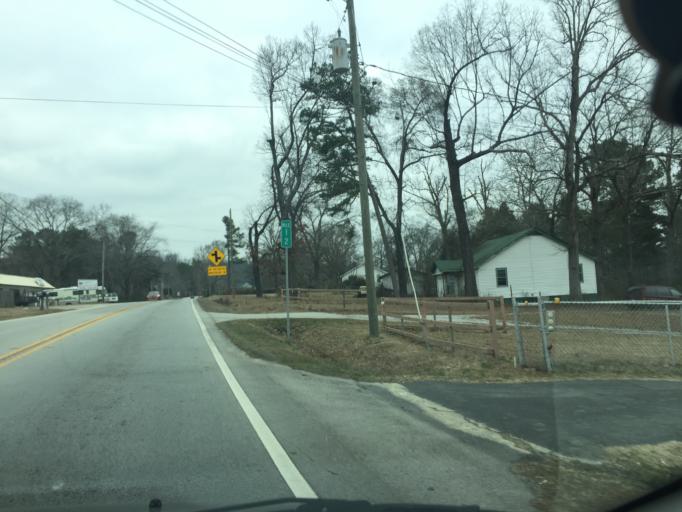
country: US
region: Georgia
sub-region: Catoosa County
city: Indian Springs
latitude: 34.9671
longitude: -85.1818
